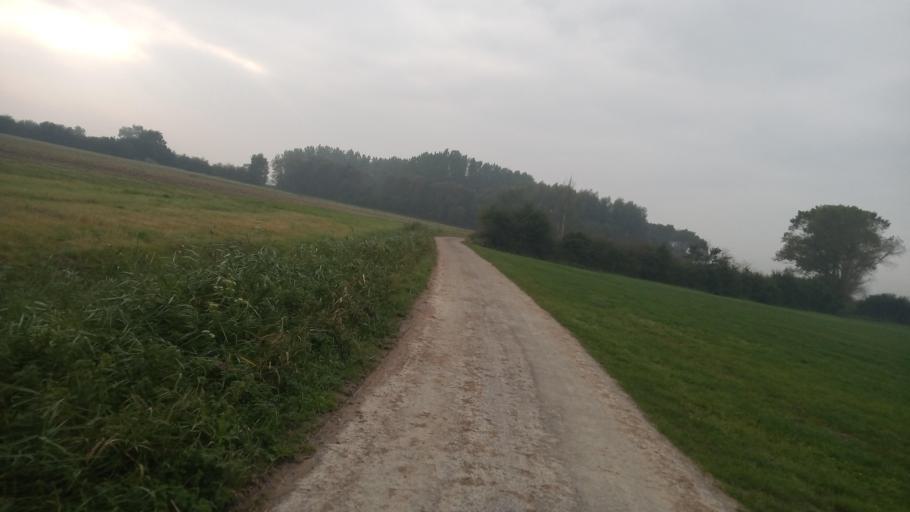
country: BE
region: Flanders
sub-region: Provincie West-Vlaanderen
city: Alveringem
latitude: 51.0317
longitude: 2.7532
